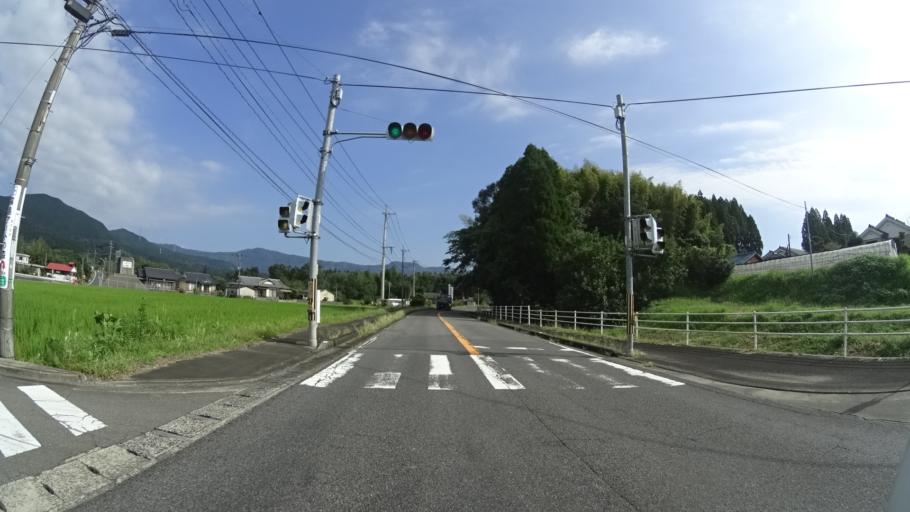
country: JP
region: Kagoshima
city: Okuchi-shinohara
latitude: 32.0340
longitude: 130.7440
